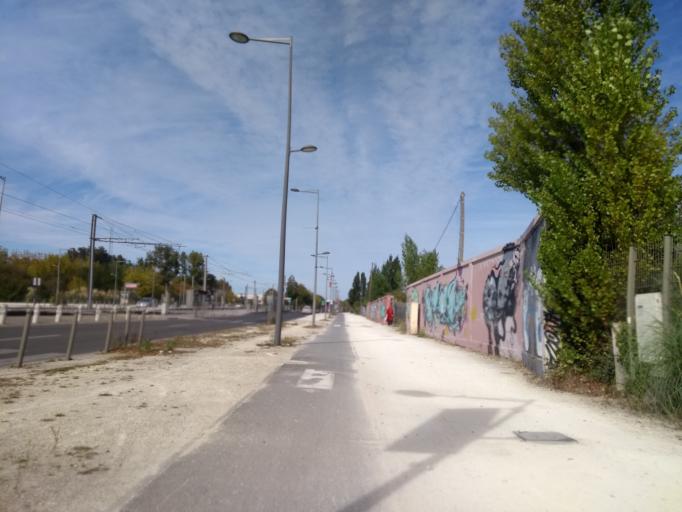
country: FR
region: Aquitaine
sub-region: Departement de la Gironde
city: Le Bouscat
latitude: 44.8703
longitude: -0.5760
